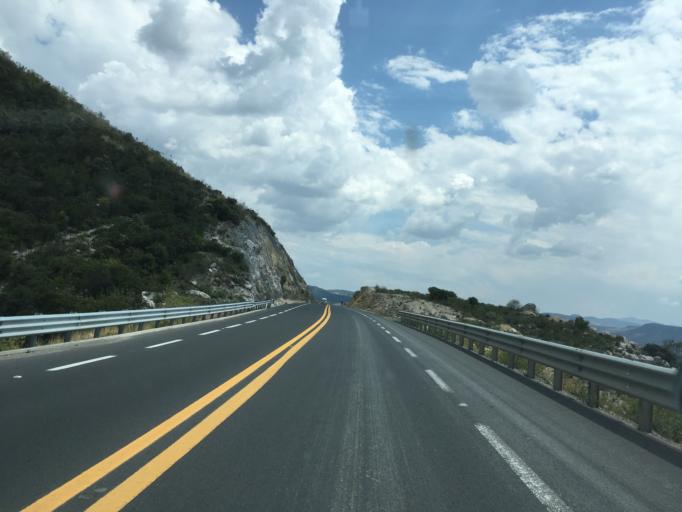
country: MX
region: Puebla
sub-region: San Jose Miahuatlan
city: San Pedro Tetitlan
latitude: 18.0135
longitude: -97.3548
